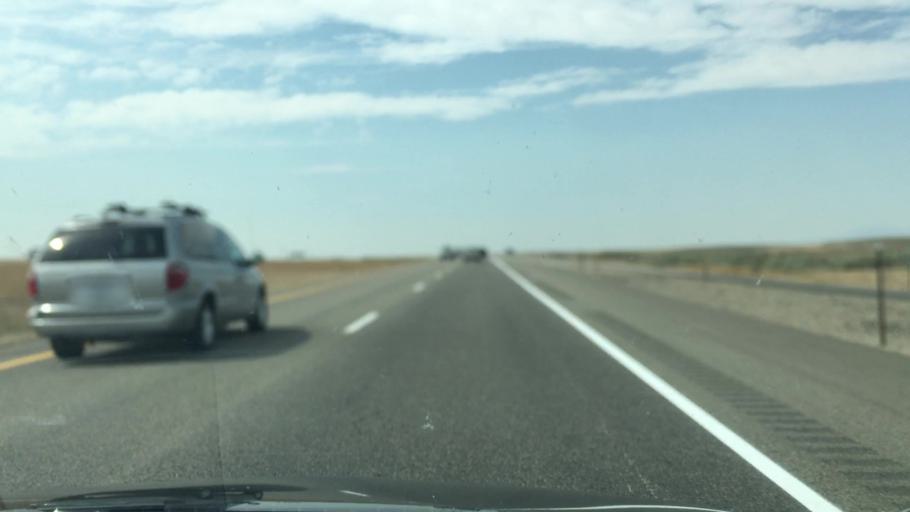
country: US
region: Idaho
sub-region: Ada County
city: Boise
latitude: 43.4673
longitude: -116.0957
